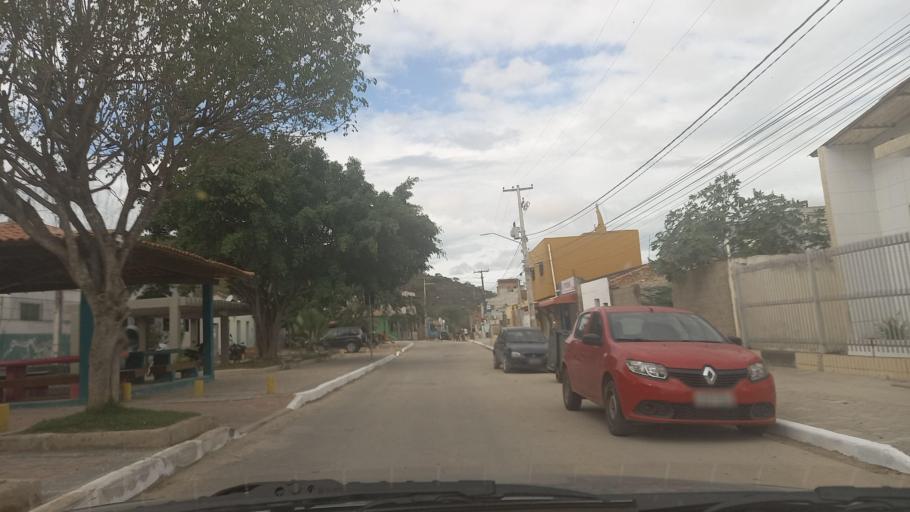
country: BR
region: Pernambuco
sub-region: Caruaru
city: Caruaru
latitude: -8.2978
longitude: -36.0295
